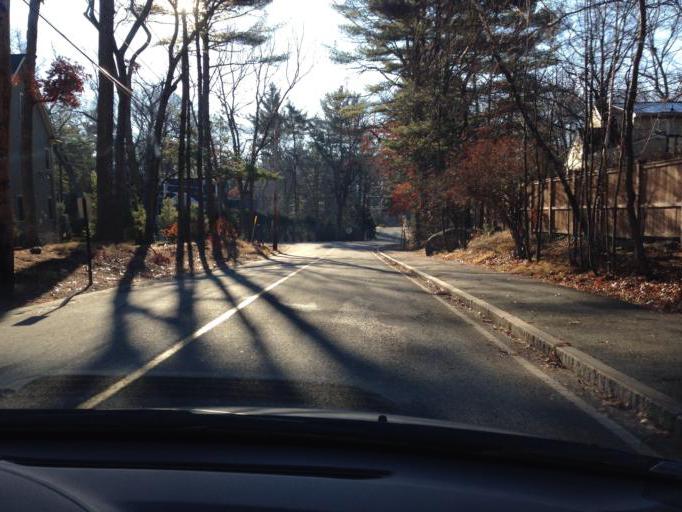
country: US
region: Massachusetts
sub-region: Middlesex County
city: Bedford
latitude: 42.5147
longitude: -71.2784
